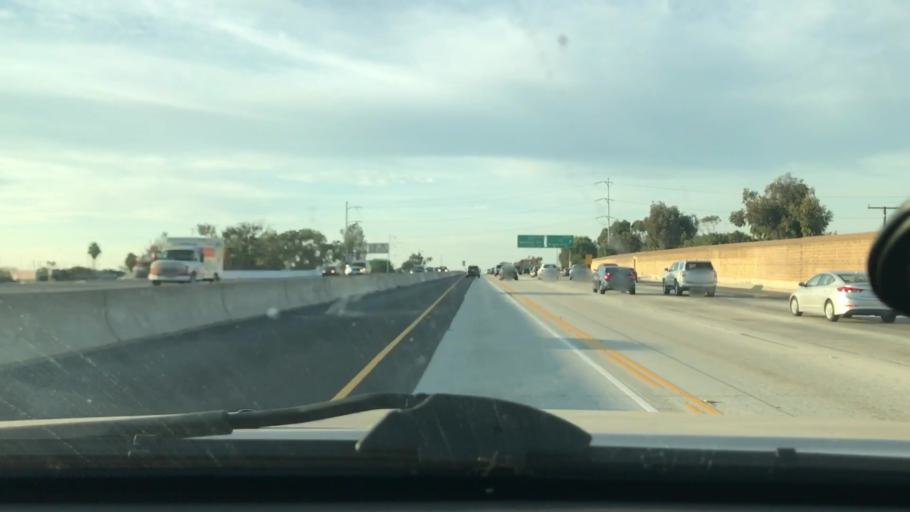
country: US
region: California
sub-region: Los Angeles County
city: Lawndale
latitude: 33.8709
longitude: -118.3408
